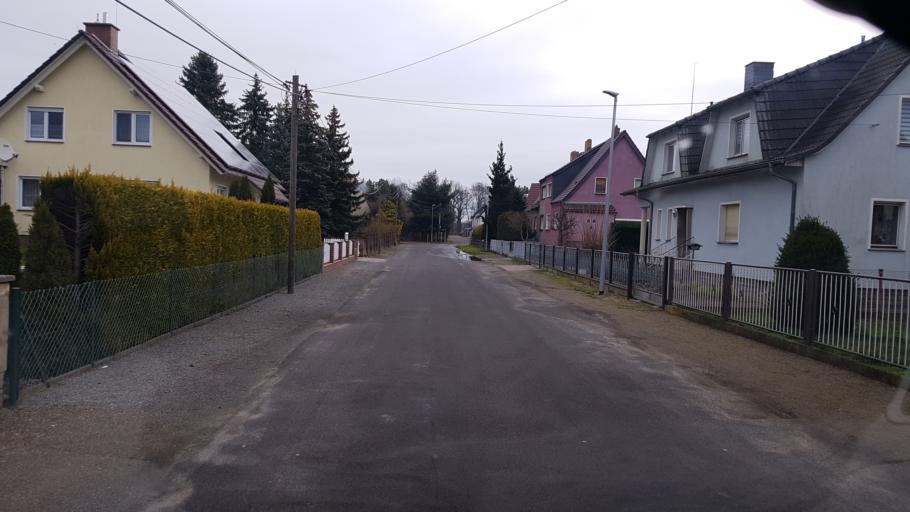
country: DE
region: Brandenburg
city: Ruhland
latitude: 51.4516
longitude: 13.8514
